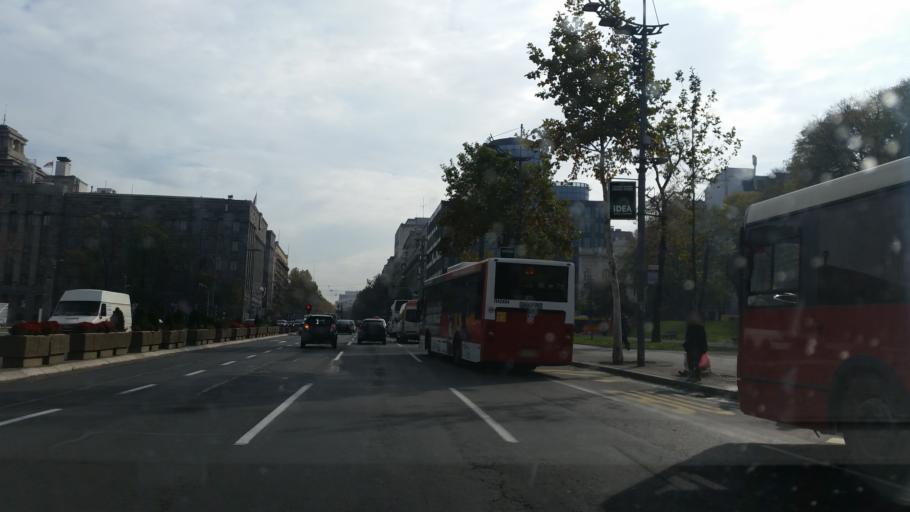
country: RS
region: Central Serbia
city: Belgrade
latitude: 44.8111
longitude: 20.4649
